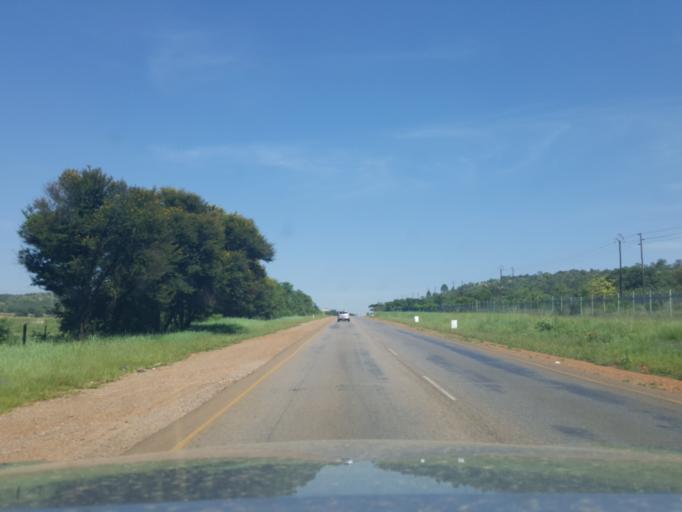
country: ZA
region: Gauteng
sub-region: City of Tshwane Metropolitan Municipality
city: Cullinan
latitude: -25.6785
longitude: 28.3553
